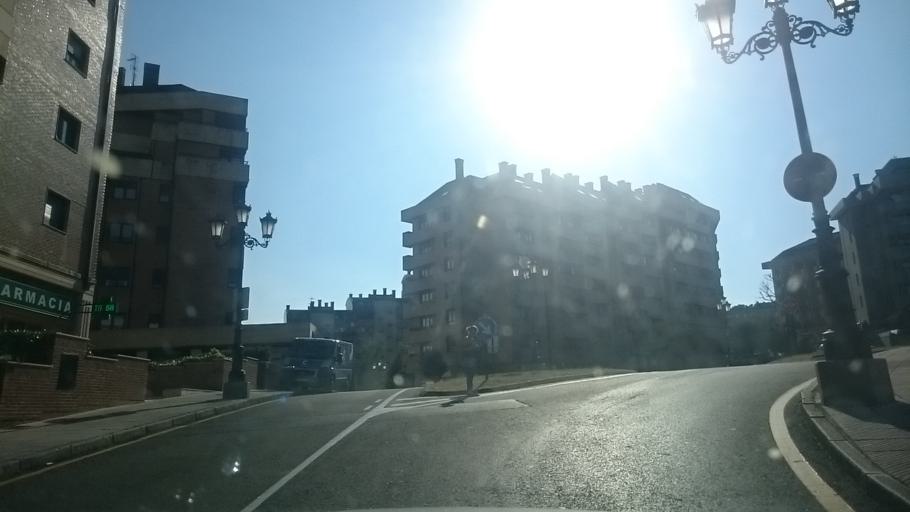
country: ES
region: Asturias
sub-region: Province of Asturias
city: Oviedo
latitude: 43.3521
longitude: -5.8650
